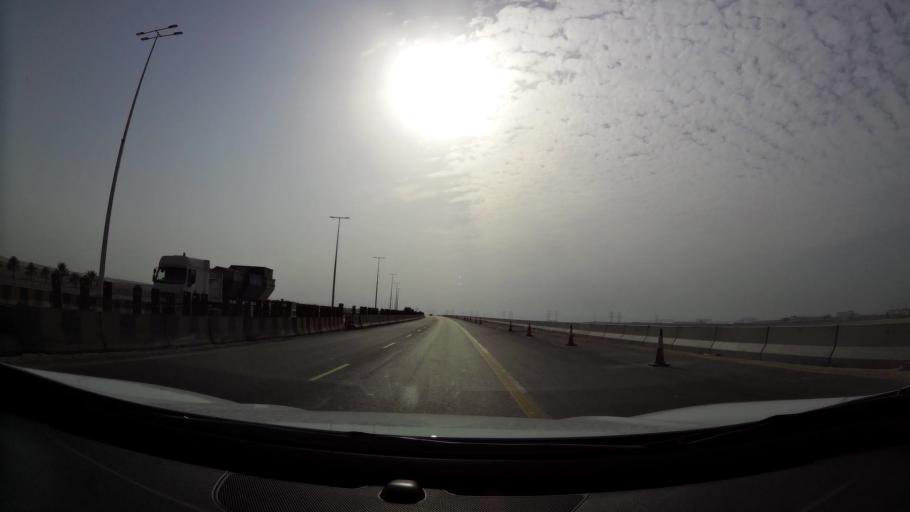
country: AE
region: Abu Dhabi
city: Abu Dhabi
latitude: 24.2704
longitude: 54.5013
